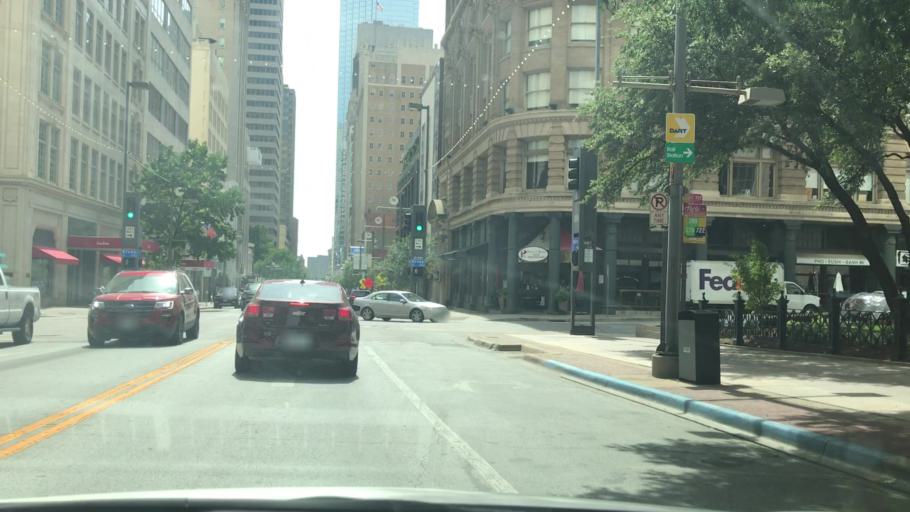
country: US
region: Texas
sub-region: Dallas County
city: Dallas
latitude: 32.7812
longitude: -96.7968
